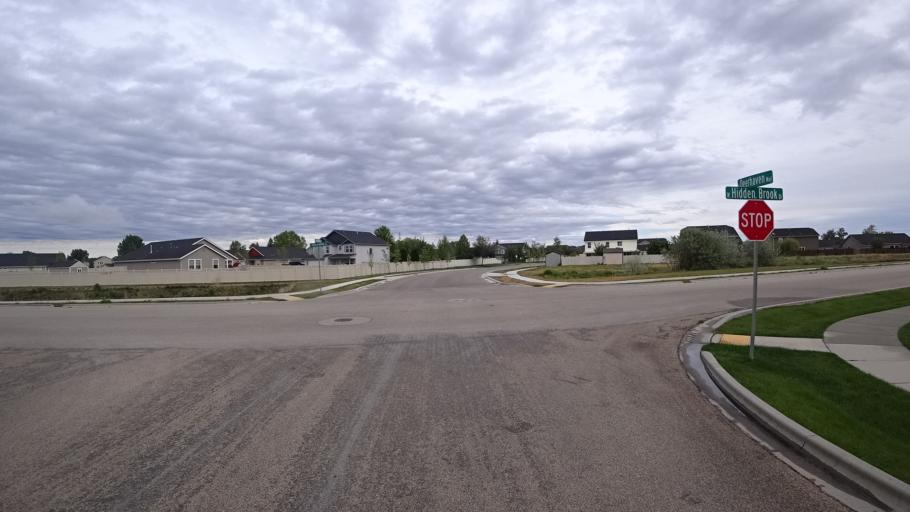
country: US
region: Idaho
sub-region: Ada County
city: Star
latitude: 43.7004
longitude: -116.5053
